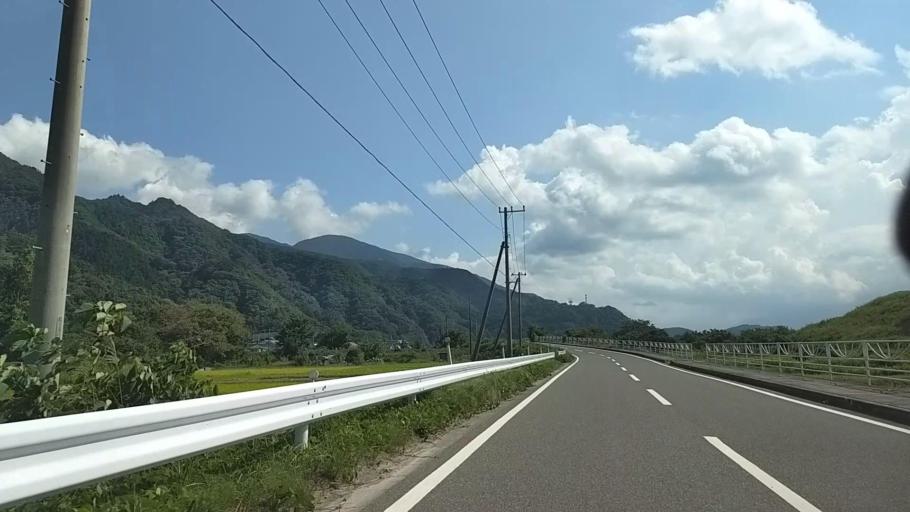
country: JP
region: Shizuoka
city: Fujinomiya
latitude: 35.3897
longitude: 138.4517
